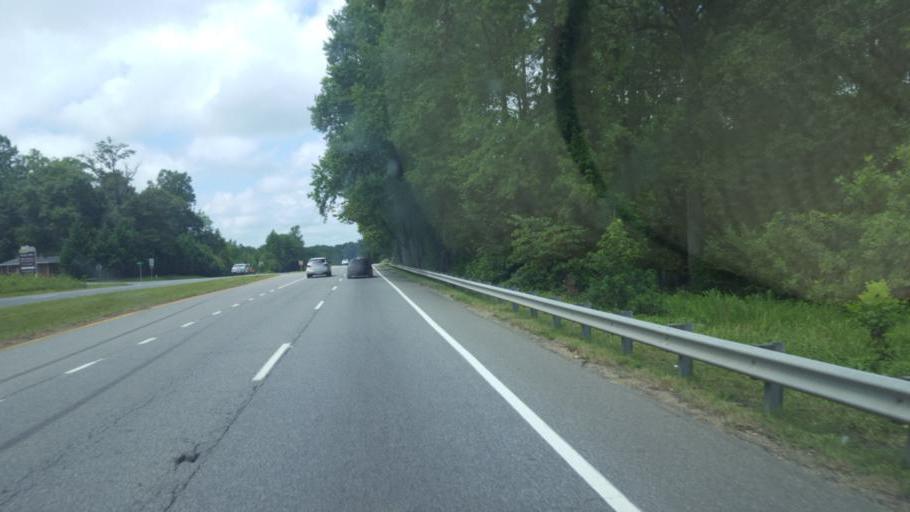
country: US
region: Virginia
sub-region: Stafford County
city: Falmouth
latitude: 38.4071
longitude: -77.5887
